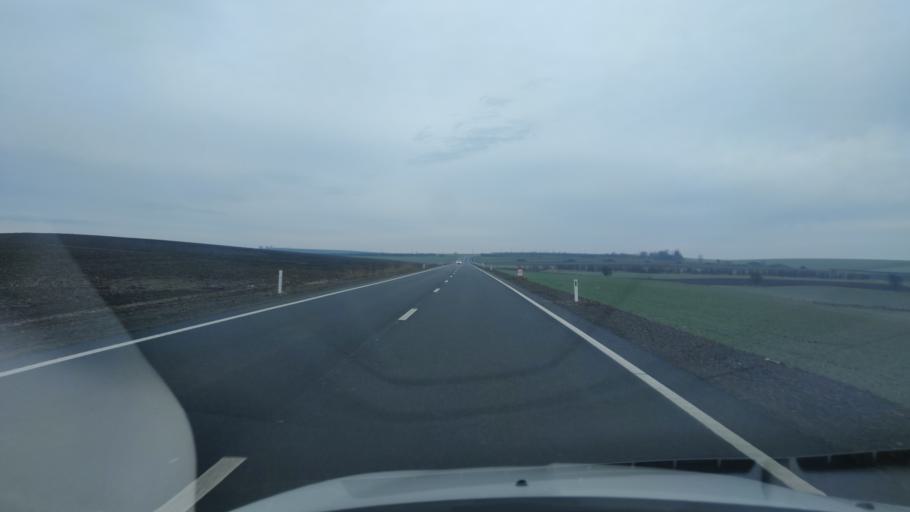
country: RO
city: Szekelyhid
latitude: 47.3303
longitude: 22.0907
